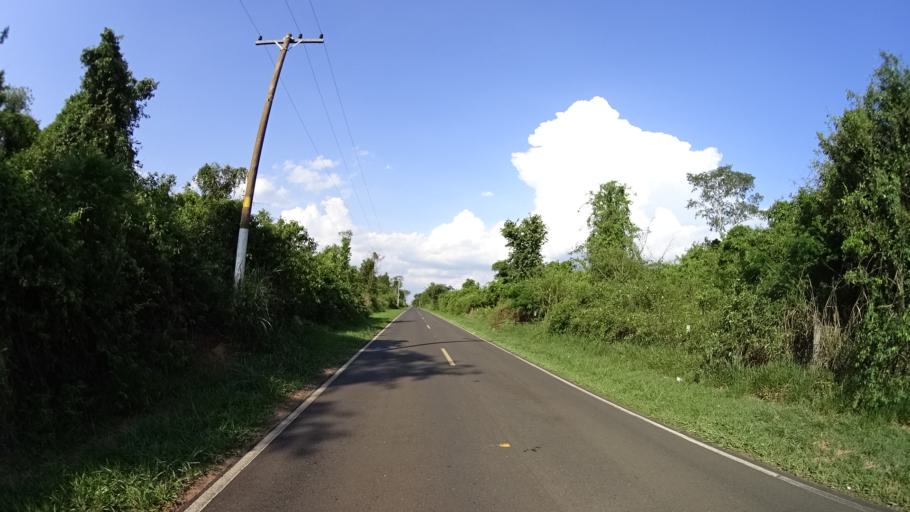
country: BR
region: Sao Paulo
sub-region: Urupes
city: Urupes
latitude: -21.3775
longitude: -49.4825
